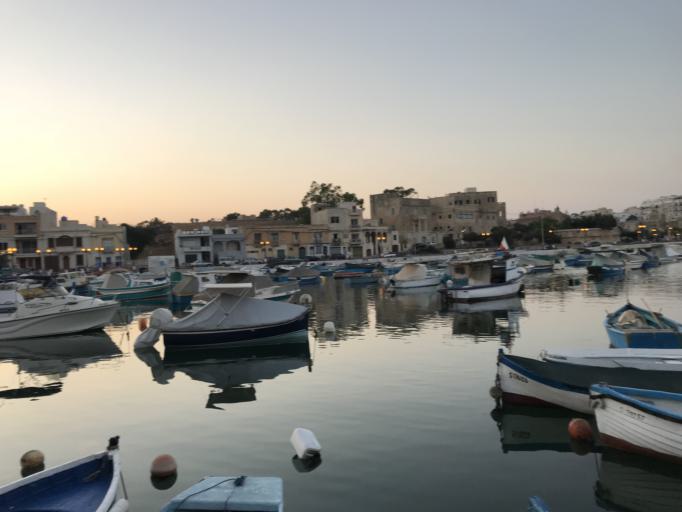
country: MT
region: Birzebbuga
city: Birzebbuga
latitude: 35.8296
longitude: 14.5308
